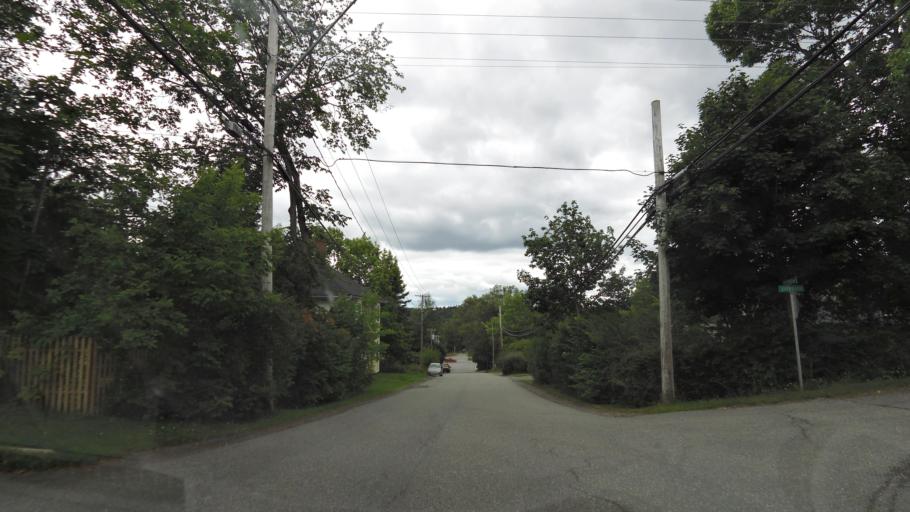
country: CA
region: New Brunswick
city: Hampton
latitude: 45.5238
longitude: -65.8261
